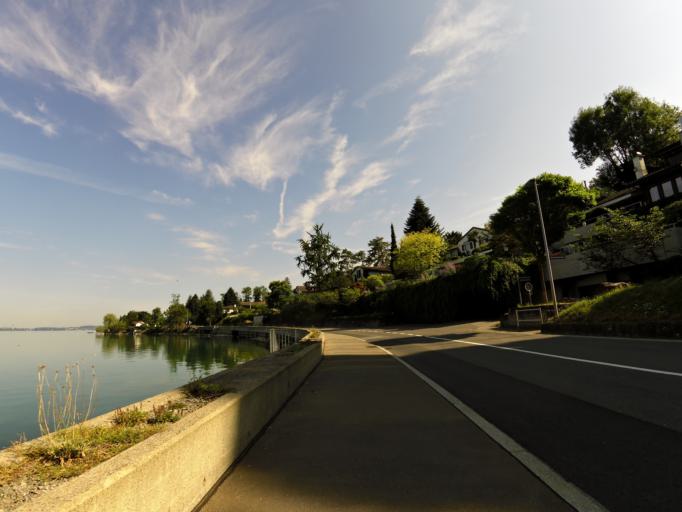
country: CH
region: Zug
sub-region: Zug
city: Walchwil
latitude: 47.1362
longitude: 8.5061
